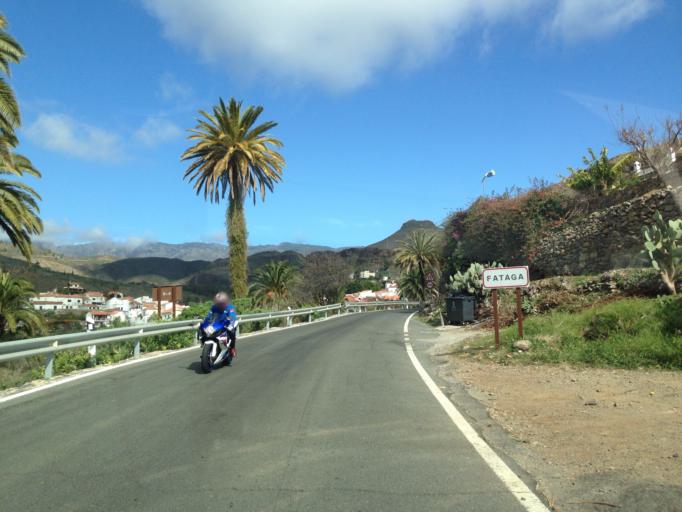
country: ES
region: Canary Islands
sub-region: Provincia de Las Palmas
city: Santa Lucia
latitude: 27.8845
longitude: -15.5651
